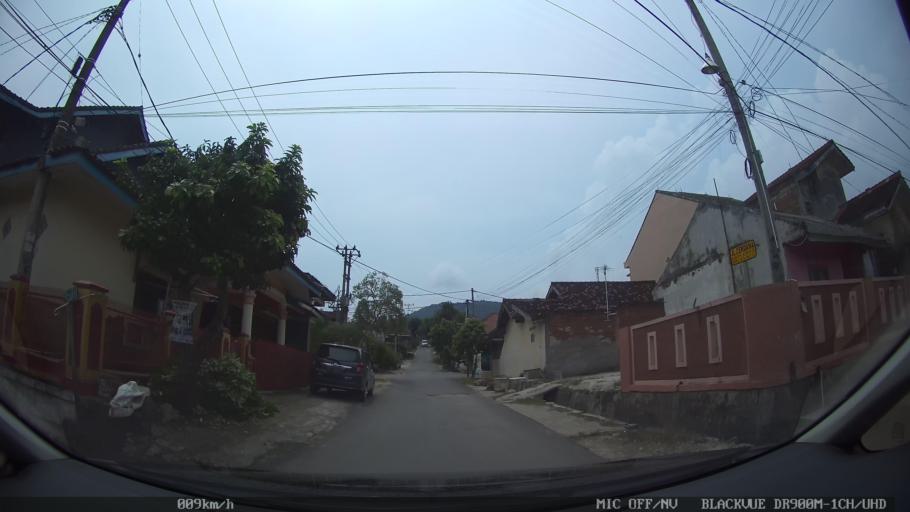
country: ID
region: Lampung
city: Kedaton
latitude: -5.4015
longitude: 105.3224
